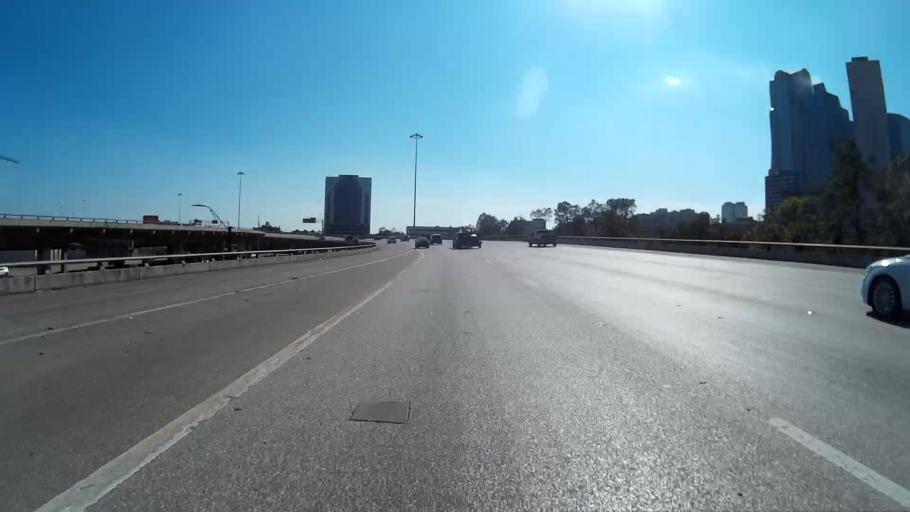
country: US
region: Texas
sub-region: Dallas County
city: Dallas
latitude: 32.7864
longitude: -96.7923
